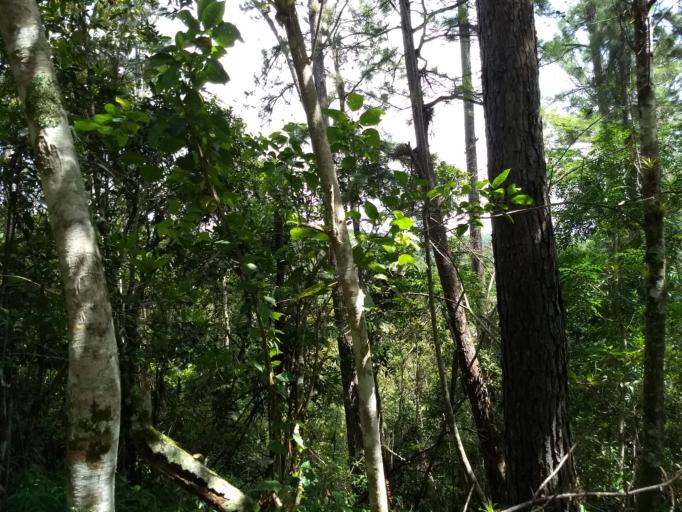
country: CU
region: Sancti Spiritus
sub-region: Municipio de Trinidad
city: Topes de Collantes
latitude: 21.9075
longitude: -80.0341
